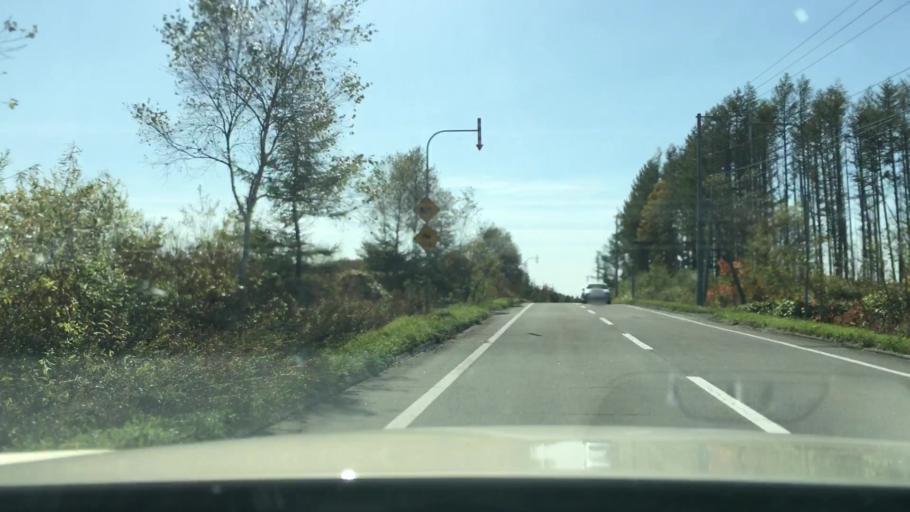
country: JP
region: Hokkaido
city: Kitami
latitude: 43.5989
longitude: 143.6825
